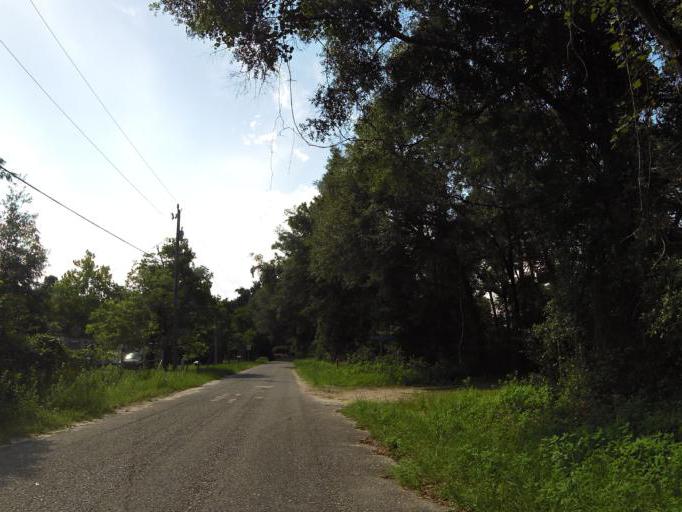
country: US
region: Florida
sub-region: Nassau County
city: Yulee
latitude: 30.6016
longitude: -81.6006
